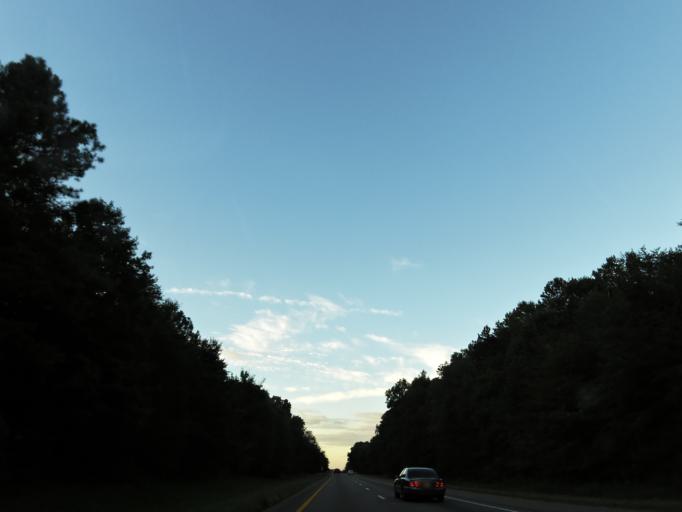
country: US
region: Tennessee
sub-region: McMinn County
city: Athens
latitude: 35.4137
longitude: -84.6989
